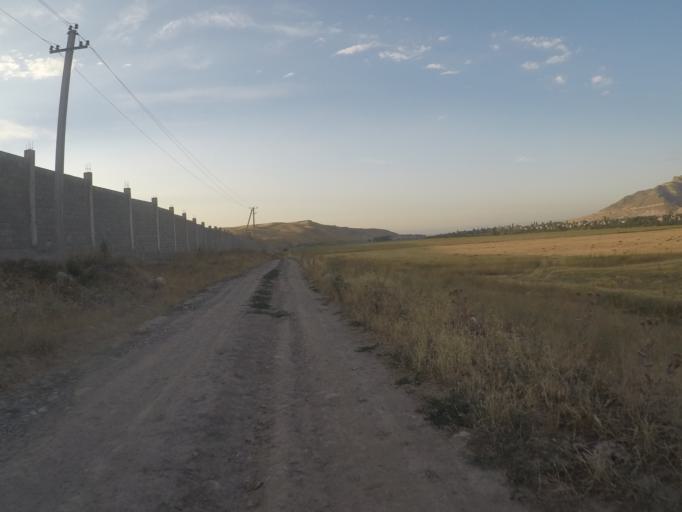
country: KG
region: Chuy
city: Bishkek
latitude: 42.7520
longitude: 74.6369
